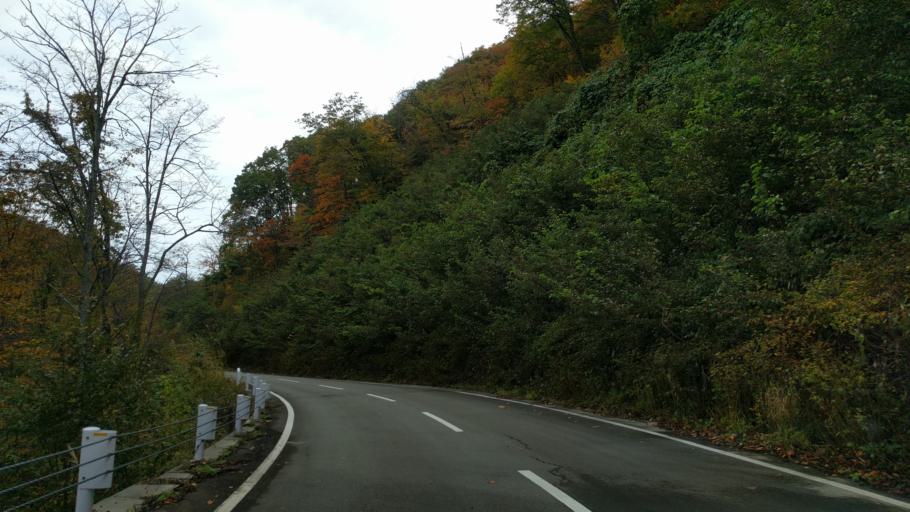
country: JP
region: Fukushima
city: Kitakata
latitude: 37.3818
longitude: 139.6973
